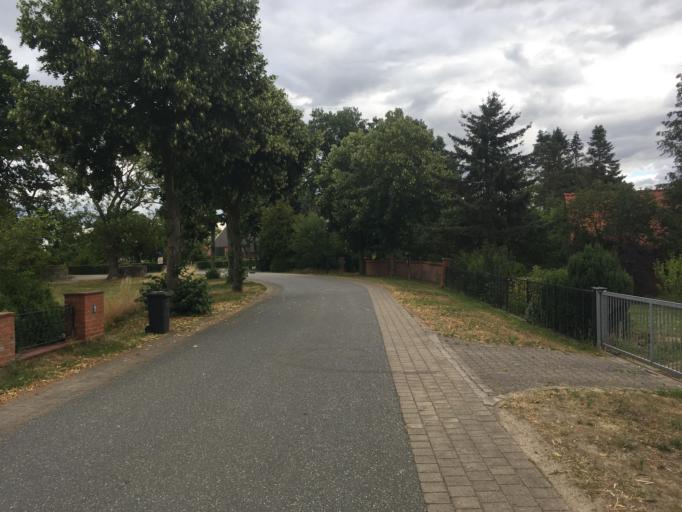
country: DE
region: Lower Saxony
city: Neu Darchau
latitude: 53.2573
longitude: 10.9209
